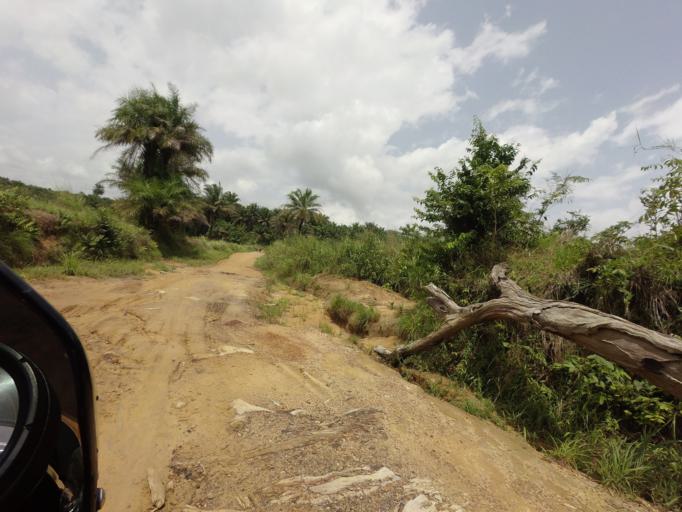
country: SL
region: Northern Province
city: Kassiri
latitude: 9.0585
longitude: -13.0581
